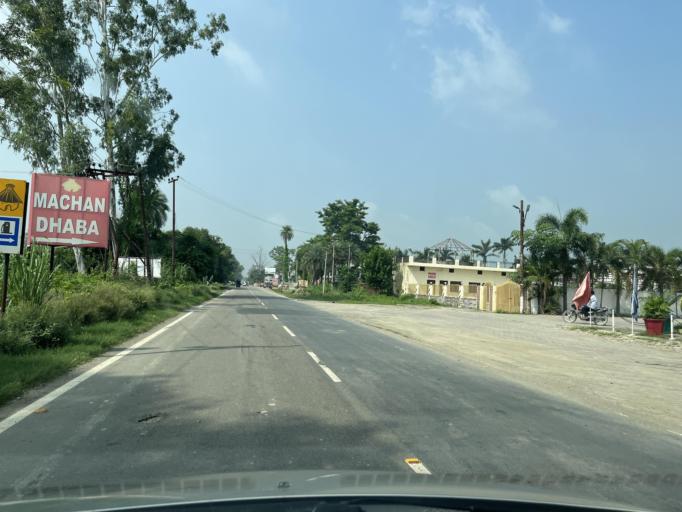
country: IN
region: Uttarakhand
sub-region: Udham Singh Nagar
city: Bazpur
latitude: 29.1719
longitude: 79.1674
